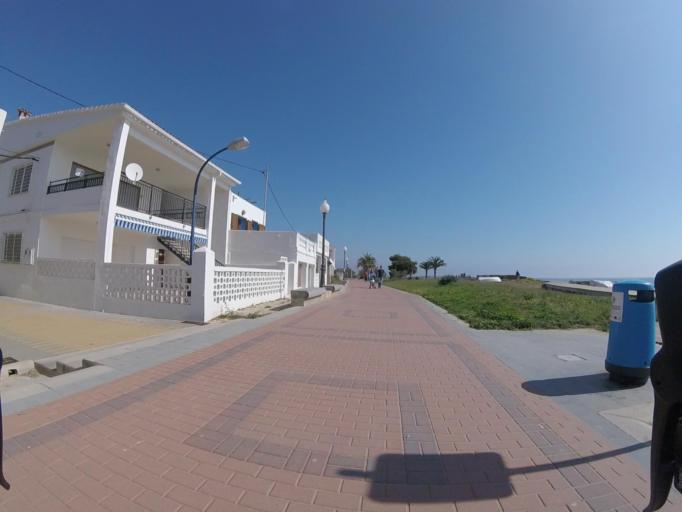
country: ES
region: Valencia
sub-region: Provincia de Castello
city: Orpesa/Oropesa del Mar
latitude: 40.1346
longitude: 0.1661
